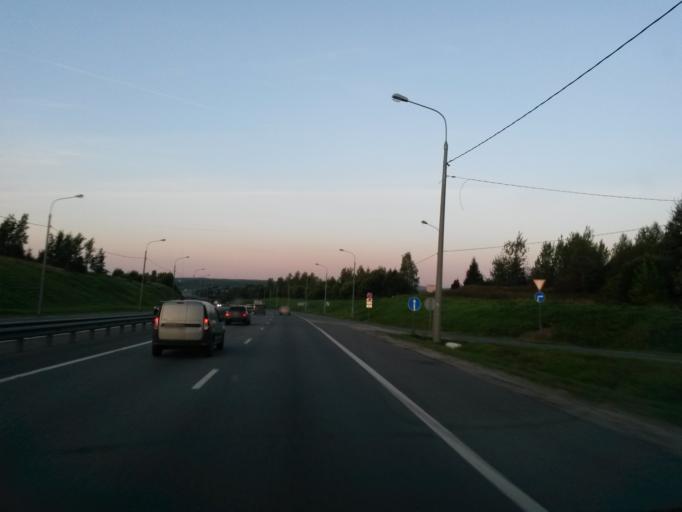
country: RU
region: Moskovskaya
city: Sergiyev Posad
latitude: 56.2862
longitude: 38.2101
